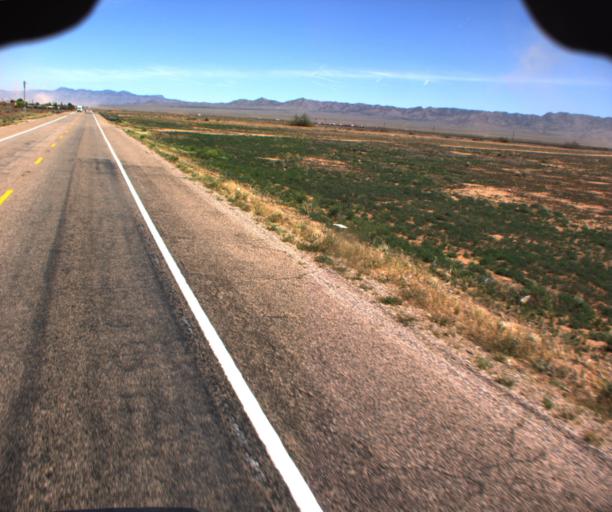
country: US
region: Arizona
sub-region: Mohave County
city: New Kingman-Butler
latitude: 35.2934
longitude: -113.9379
